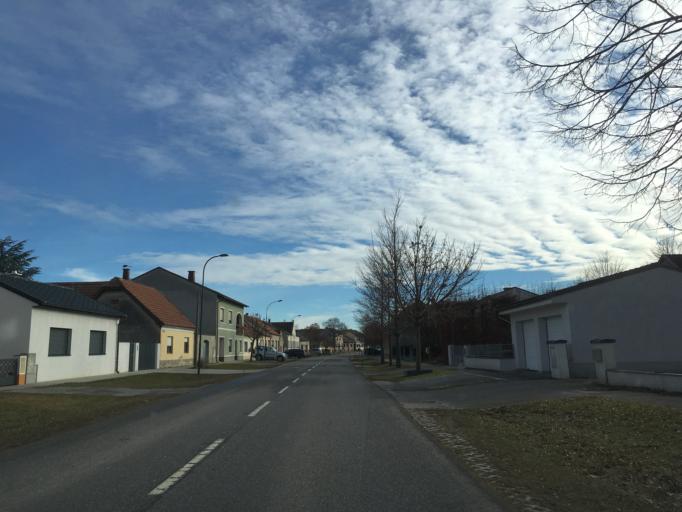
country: AT
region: Burgenland
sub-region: Politischer Bezirk Neusiedl am See
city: Pama
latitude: 48.0527
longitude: 17.0277
